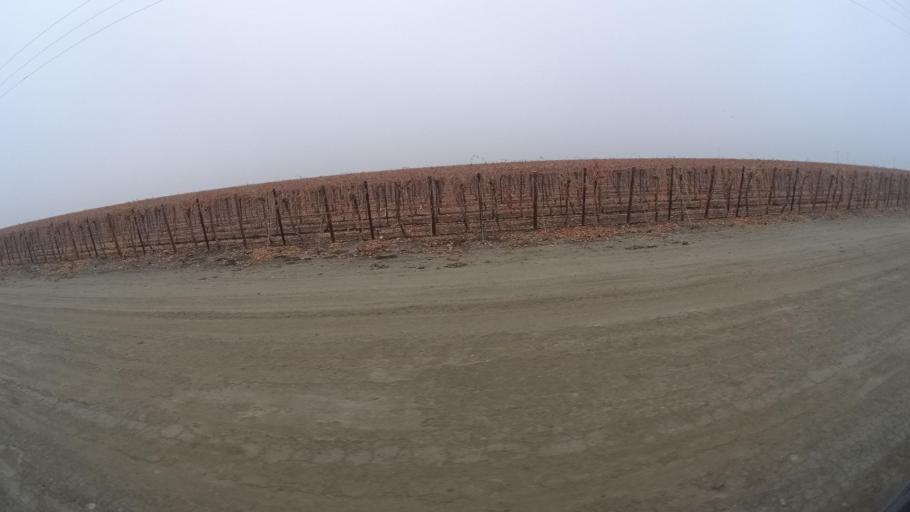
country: US
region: California
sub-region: Kern County
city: Buttonwillow
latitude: 35.4647
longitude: -119.5649
